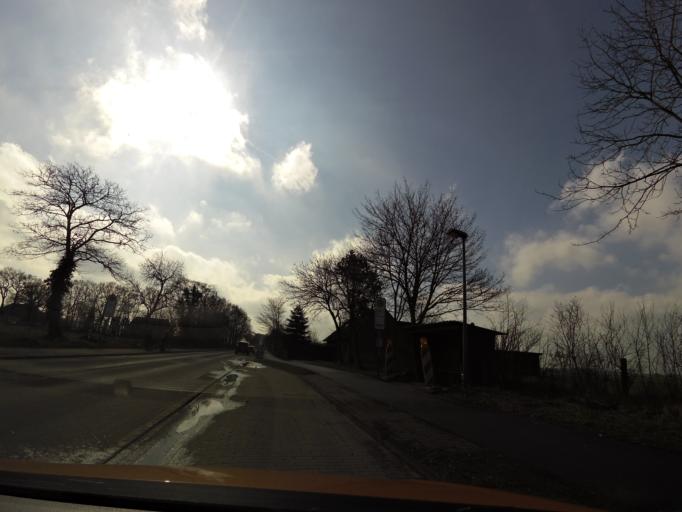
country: DE
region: Lower Saxony
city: Varel
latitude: 53.4386
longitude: 8.1187
